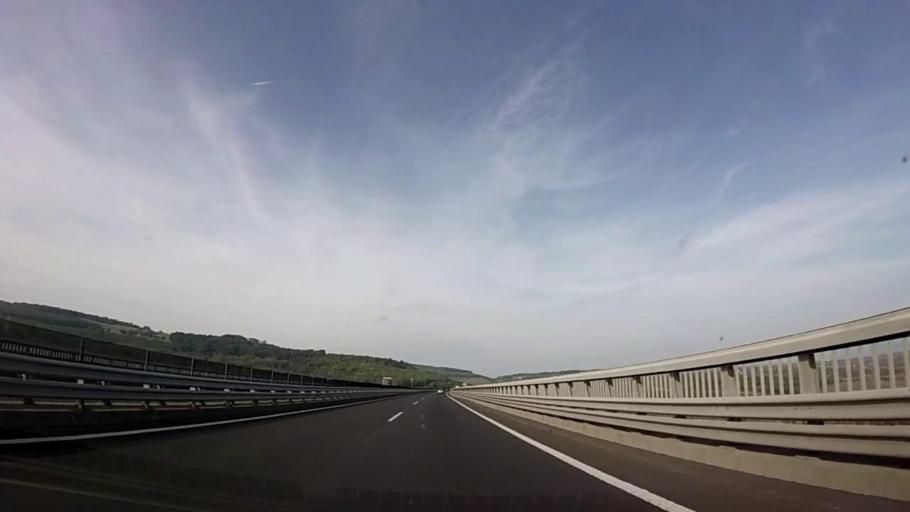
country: HU
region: Somogy
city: Balatonfoldvar
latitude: 46.8174
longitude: 17.8978
